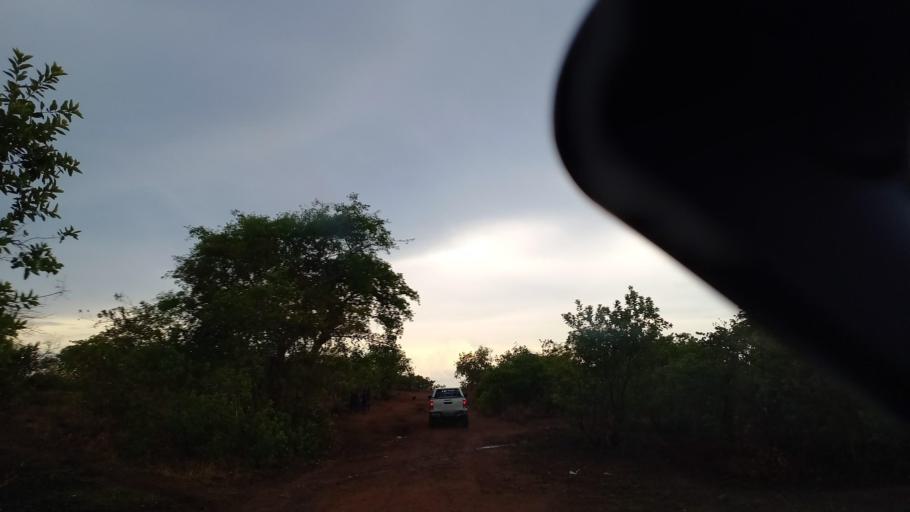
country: ZM
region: Lusaka
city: Kafue
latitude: -16.0214
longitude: 28.2943
